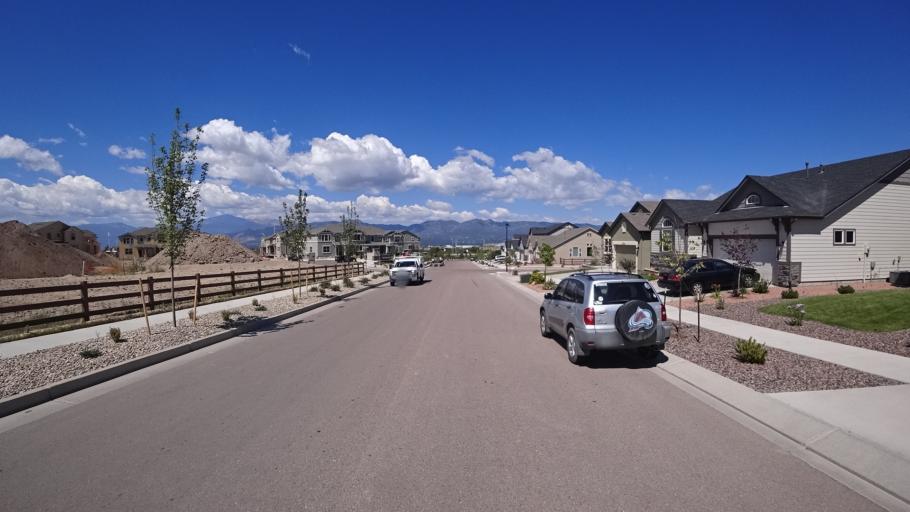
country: US
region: Colorado
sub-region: El Paso County
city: Black Forest
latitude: 38.9892
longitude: -104.7670
